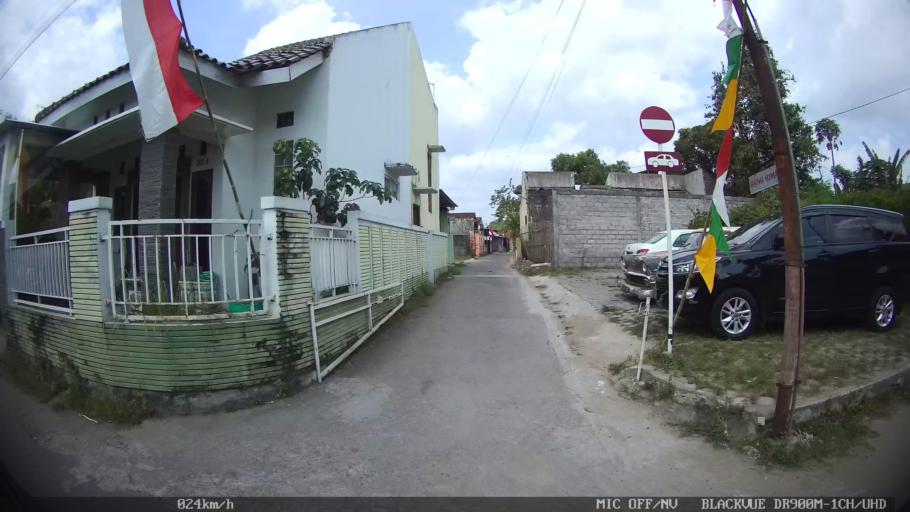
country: ID
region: Daerah Istimewa Yogyakarta
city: Gamping Lor
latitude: -7.8030
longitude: 110.3382
